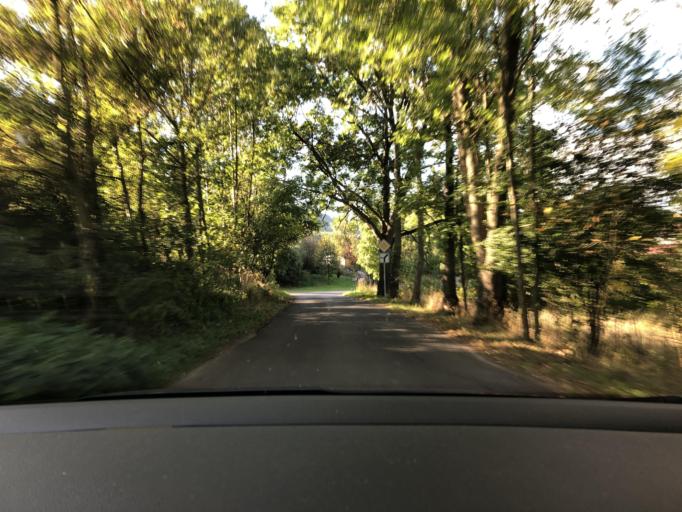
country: CZ
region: Ustecky
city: Zitenice
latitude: 50.5715
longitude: 14.1843
